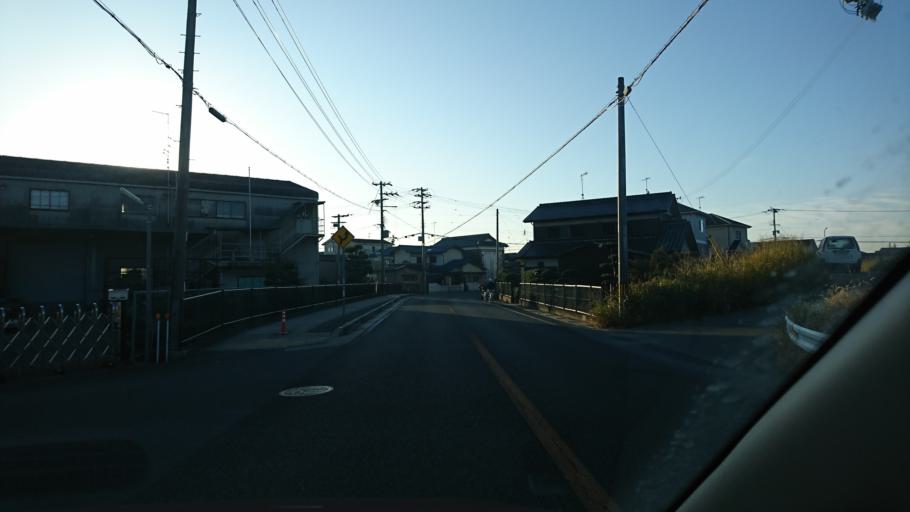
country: JP
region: Hyogo
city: Shirahamacho-usazakiminami
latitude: 34.7840
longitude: 134.7715
